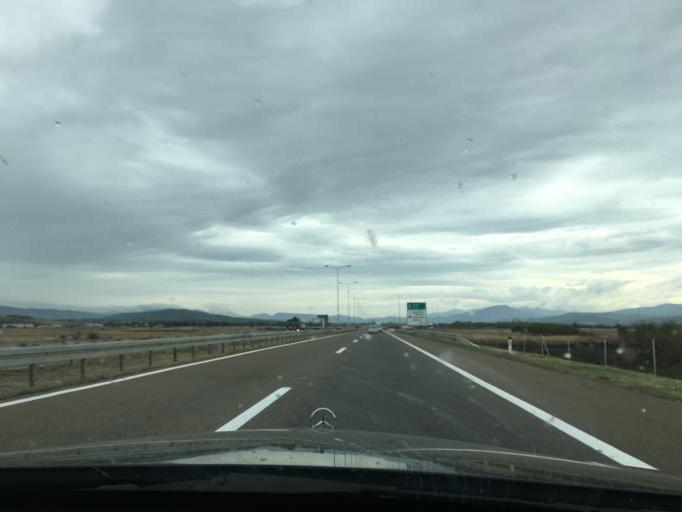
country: RS
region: Central Serbia
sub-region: Nisavski Okrug
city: Nis
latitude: 43.3539
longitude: 21.8363
